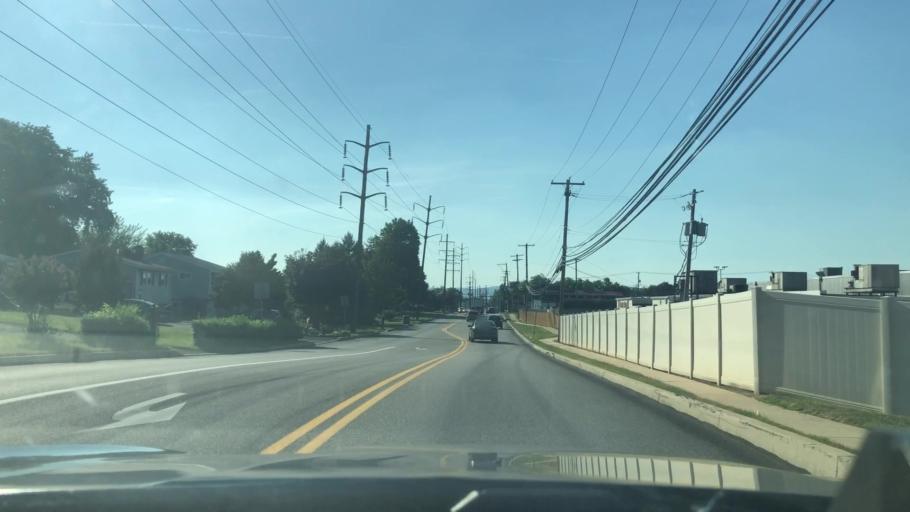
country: US
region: Pennsylvania
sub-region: Cumberland County
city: Shiremanstown
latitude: 40.2170
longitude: -76.9756
